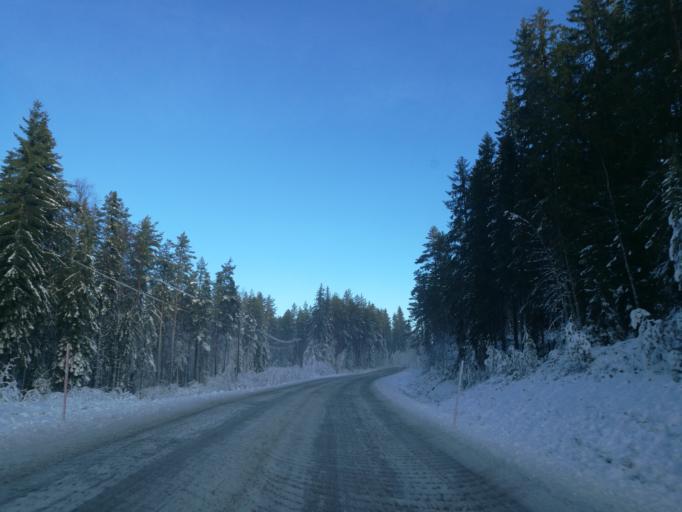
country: NO
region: Hedmark
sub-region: Grue
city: Kirkenaer
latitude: 60.3840
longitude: 12.3591
